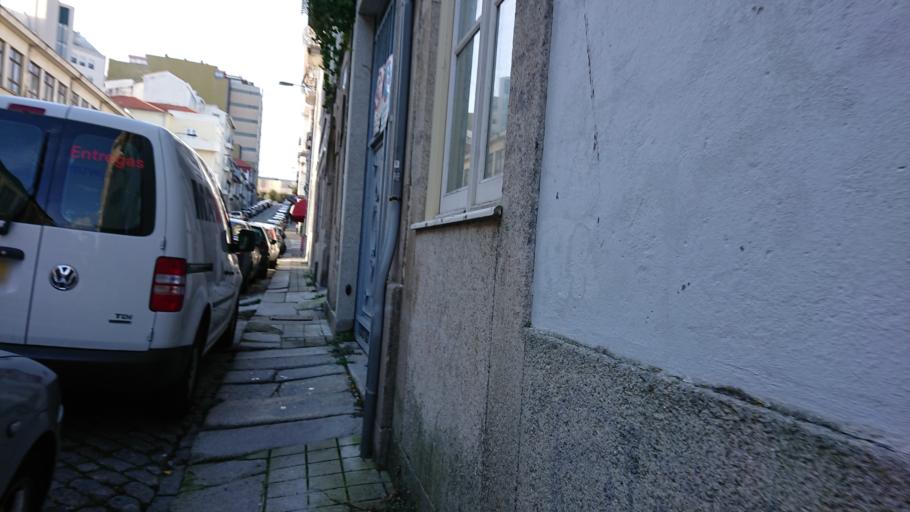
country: PT
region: Porto
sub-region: Porto
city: Porto
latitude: 41.1535
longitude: -8.6248
